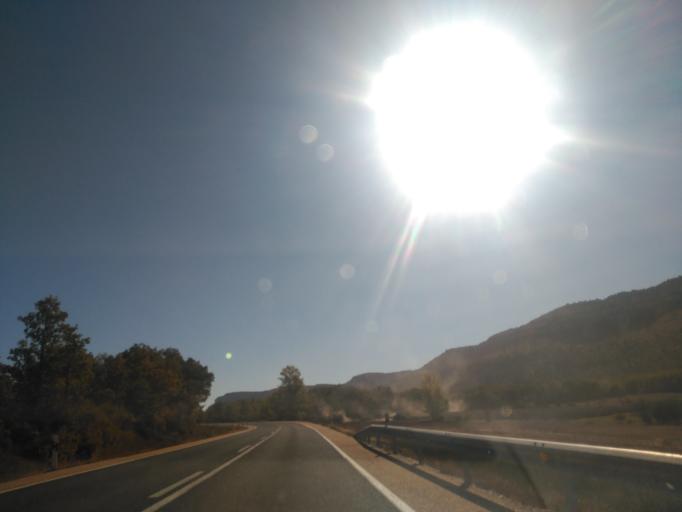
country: ES
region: Castille and Leon
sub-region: Provincia de Soria
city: Cidones
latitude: 41.8118
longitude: -2.7042
